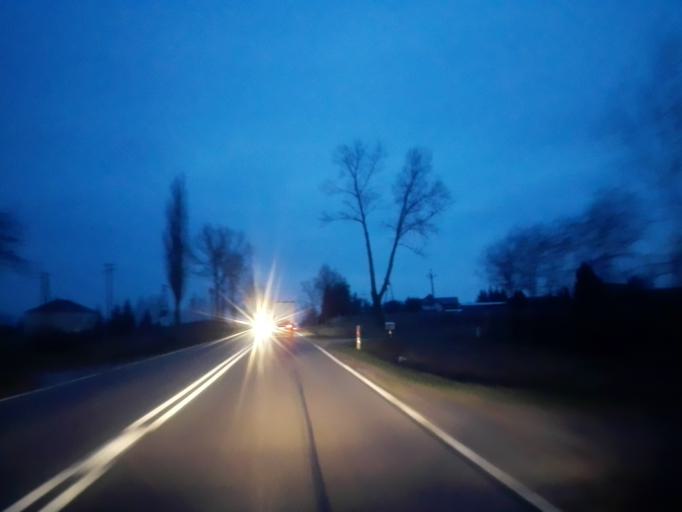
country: PL
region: Podlasie
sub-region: Lomza
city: Lomza
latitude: 53.1097
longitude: 22.0290
